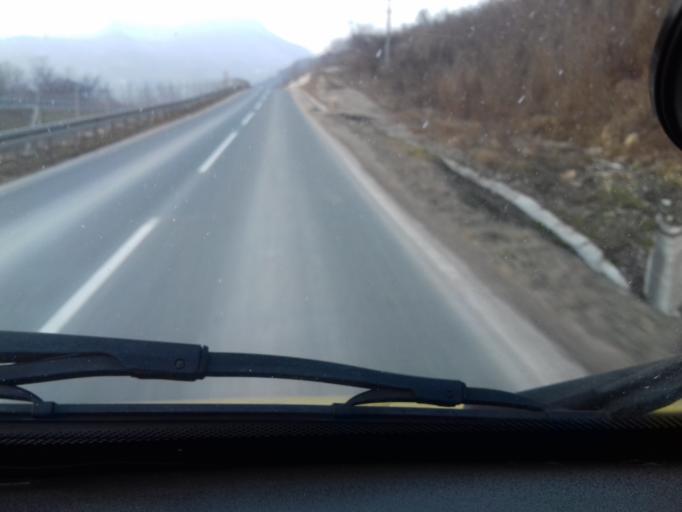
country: BA
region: Federation of Bosnia and Herzegovina
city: Kakanj
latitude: 44.1300
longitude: 18.0877
